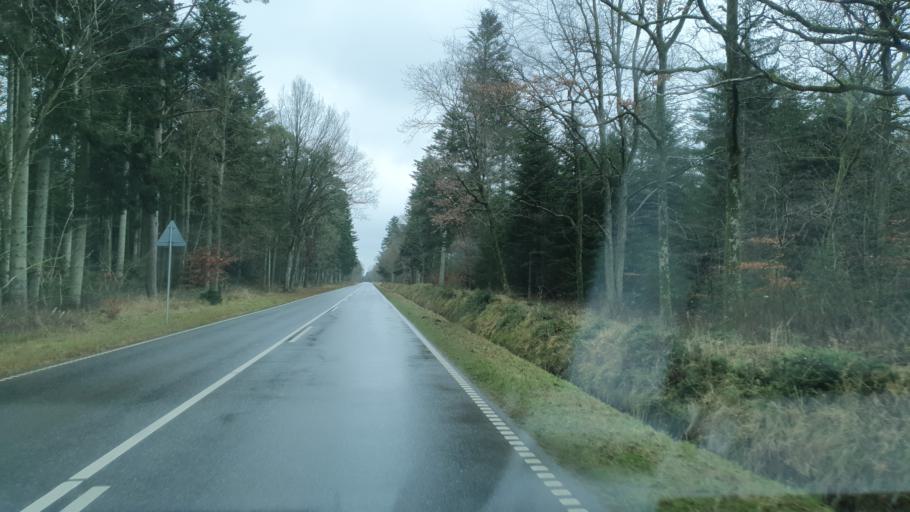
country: DK
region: North Denmark
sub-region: Jammerbugt Kommune
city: Fjerritslev
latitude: 57.1208
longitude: 9.1266
